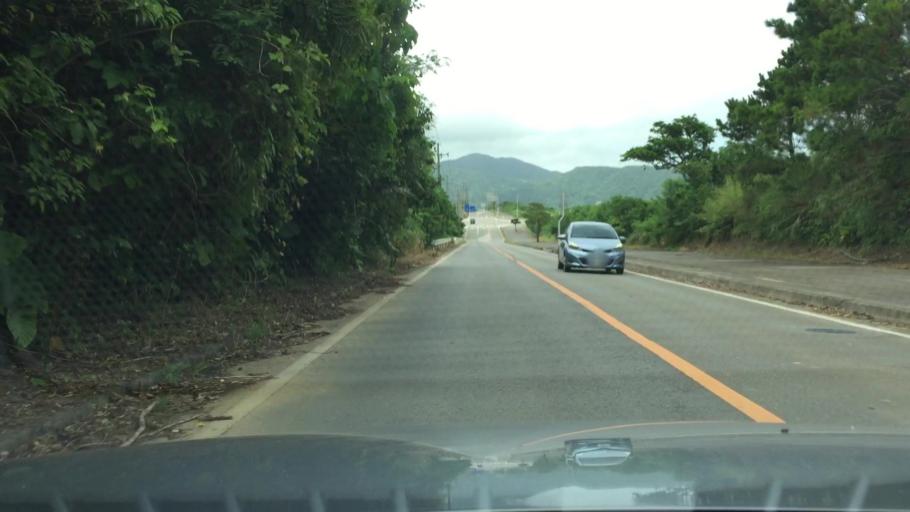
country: JP
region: Okinawa
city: Ishigaki
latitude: 24.4081
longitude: 124.2131
